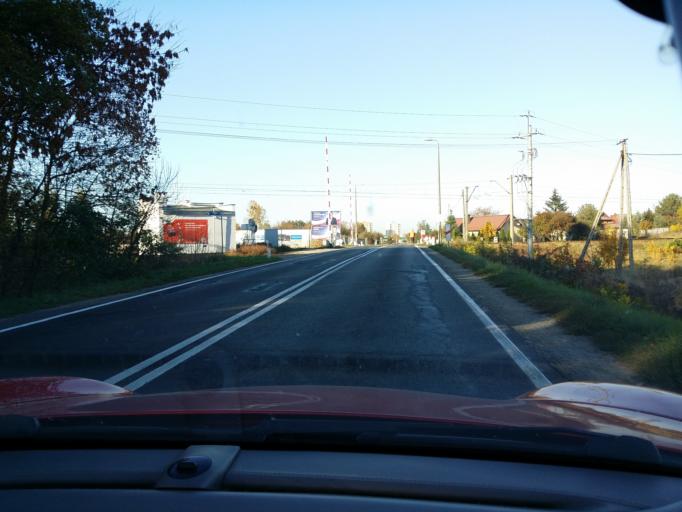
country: PL
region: Masovian Voivodeship
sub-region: Powiat radomski
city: Trablice
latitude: 51.3545
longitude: 21.1293
